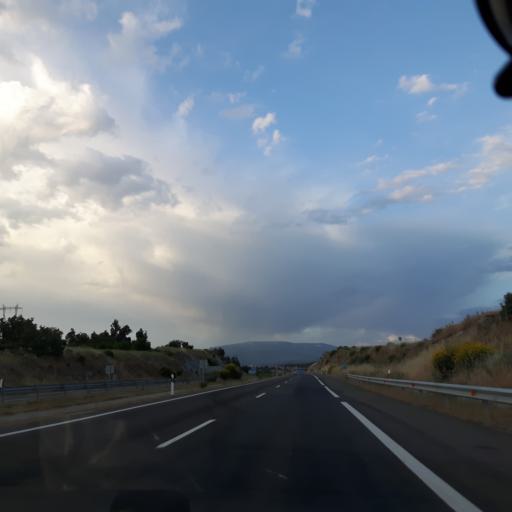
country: ES
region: Castille and Leon
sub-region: Provincia de Salamanca
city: Fuentes de Bejar
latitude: 40.5166
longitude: -5.6734
